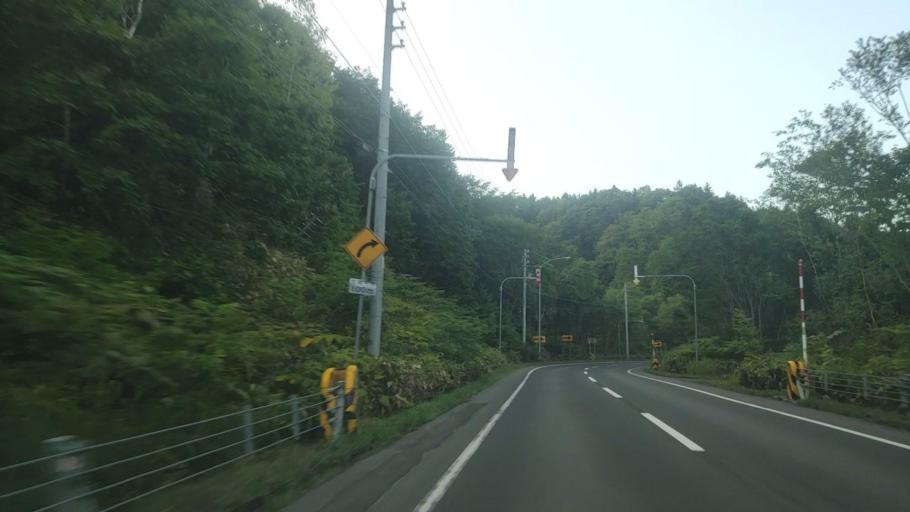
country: JP
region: Hokkaido
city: Bibai
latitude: 43.2514
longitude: 142.0241
